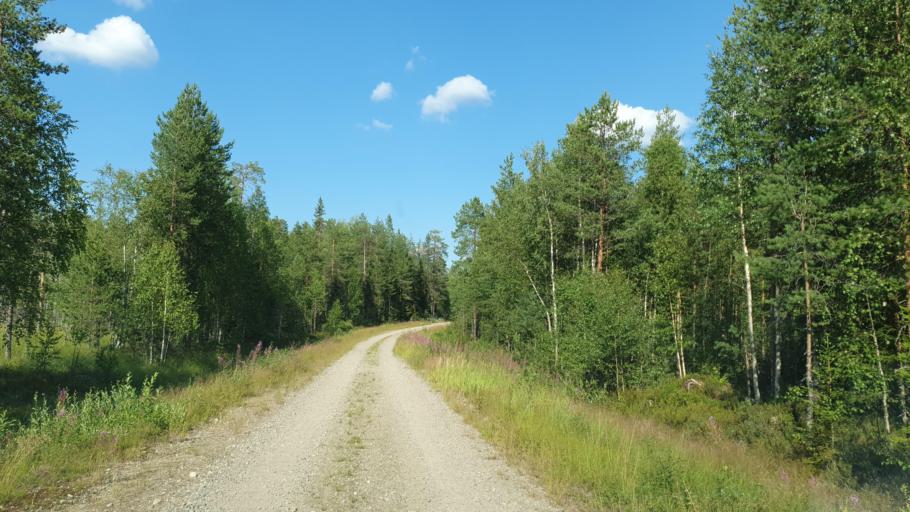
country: FI
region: Kainuu
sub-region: Kehys-Kainuu
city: Kuhmo
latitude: 63.9634
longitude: 29.5396
